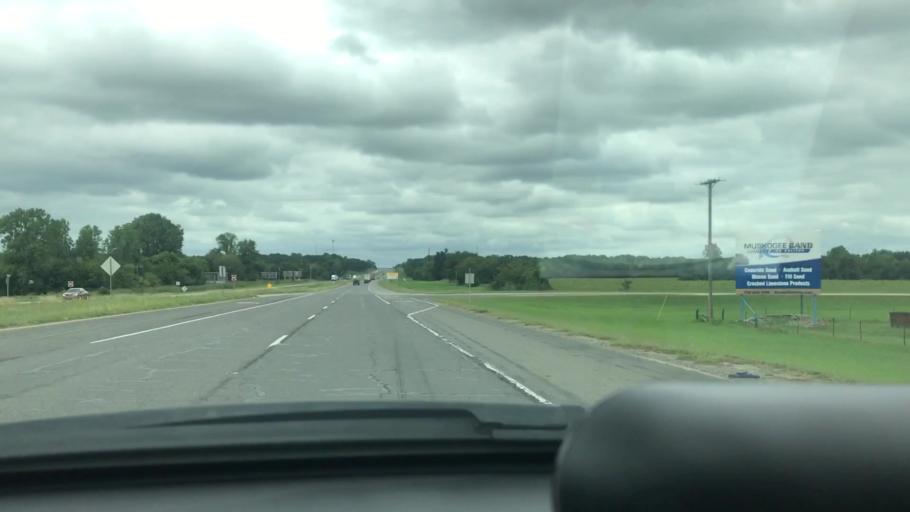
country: US
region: Oklahoma
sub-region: Muskogee County
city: Muskogee
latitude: 35.8122
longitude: -95.4023
